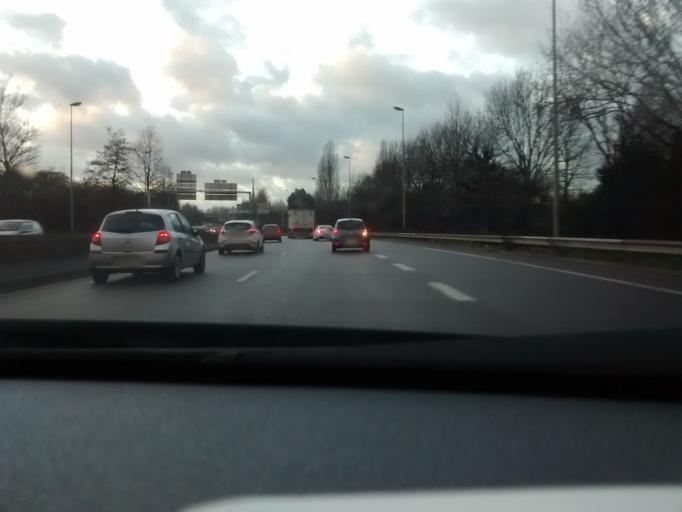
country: FR
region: Haute-Normandie
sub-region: Departement de la Seine-Maritime
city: Bihorel
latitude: 49.4387
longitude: 1.1206
